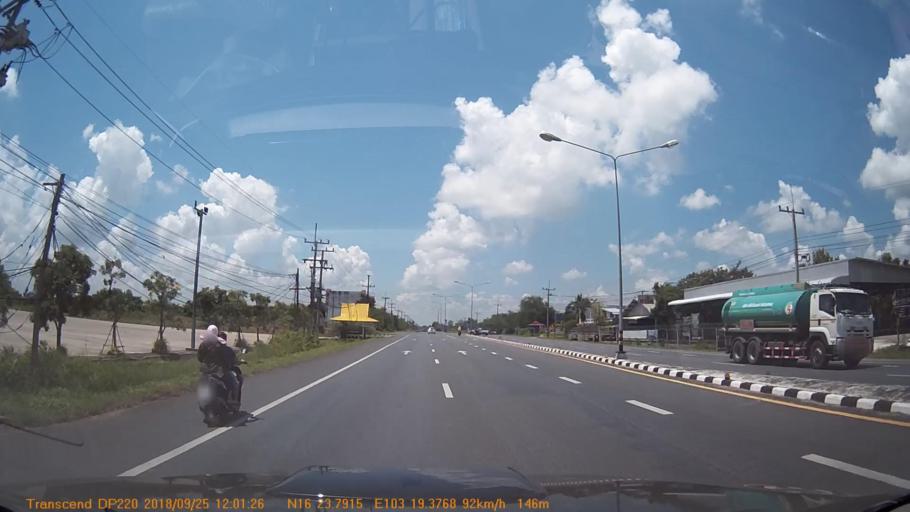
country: TH
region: Kalasin
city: Yang Talat
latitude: 16.3965
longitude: 103.3230
